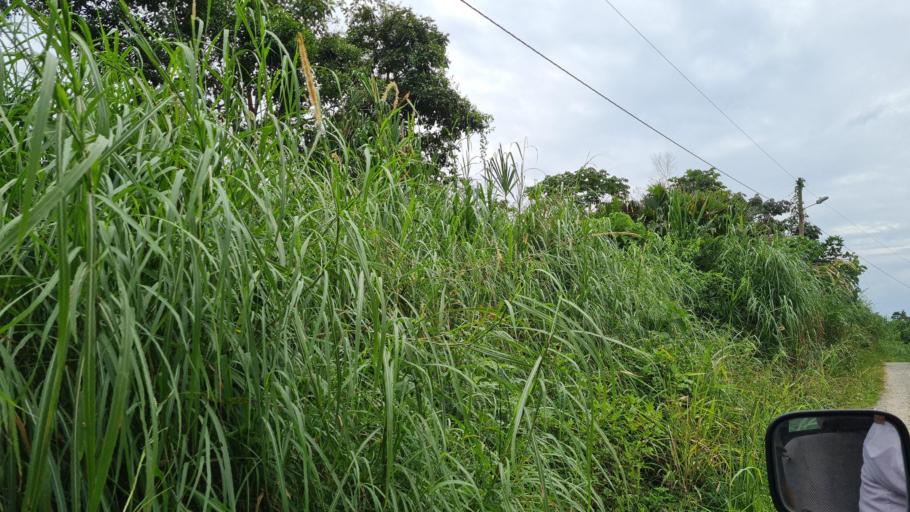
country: EC
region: Napo
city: Tena
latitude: -0.9981
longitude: -77.7546
